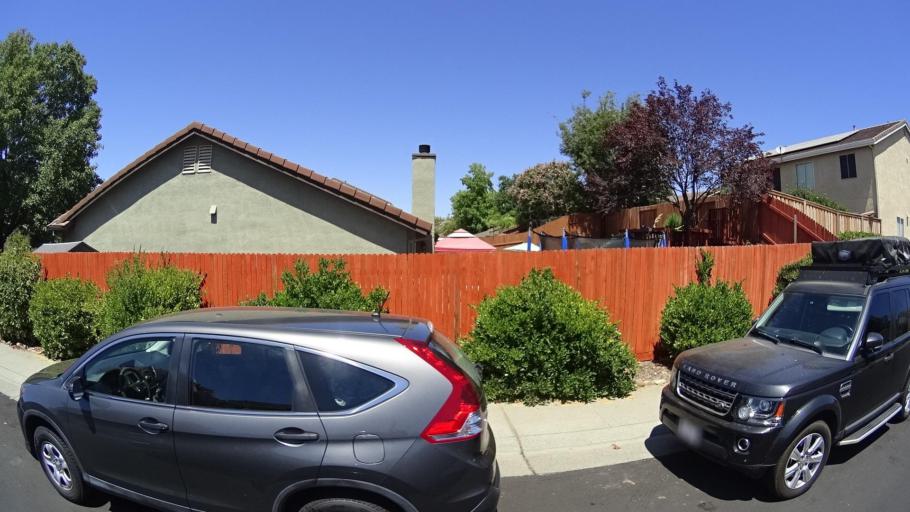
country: US
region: California
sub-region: Placer County
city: Rocklin
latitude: 38.8165
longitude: -121.2720
